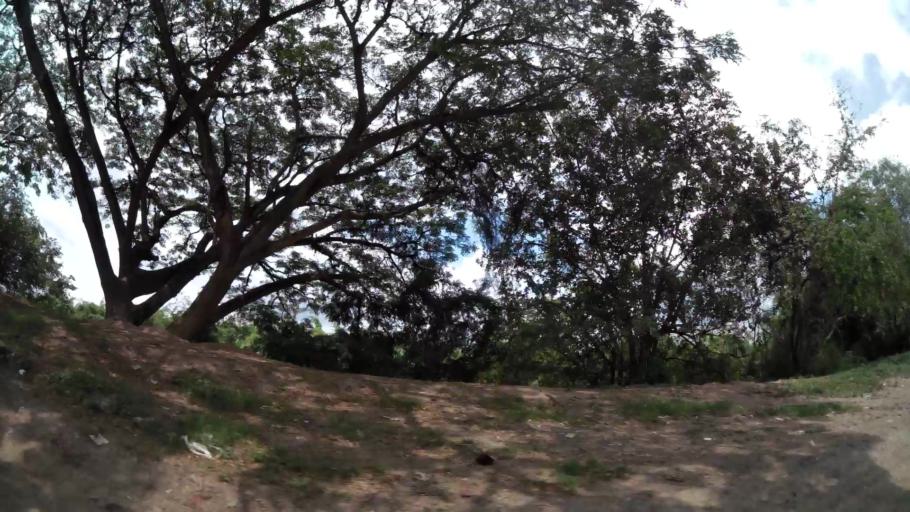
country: CO
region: Valle del Cauca
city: Cali
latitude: 3.4946
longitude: -76.4831
